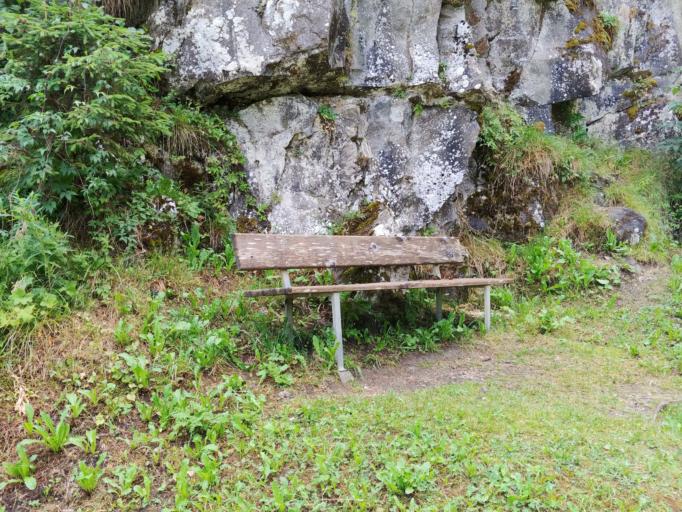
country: IT
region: Trentino-Alto Adige
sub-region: Bolzano
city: Santa Cristina Valgardena
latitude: 46.5557
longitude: 11.7193
